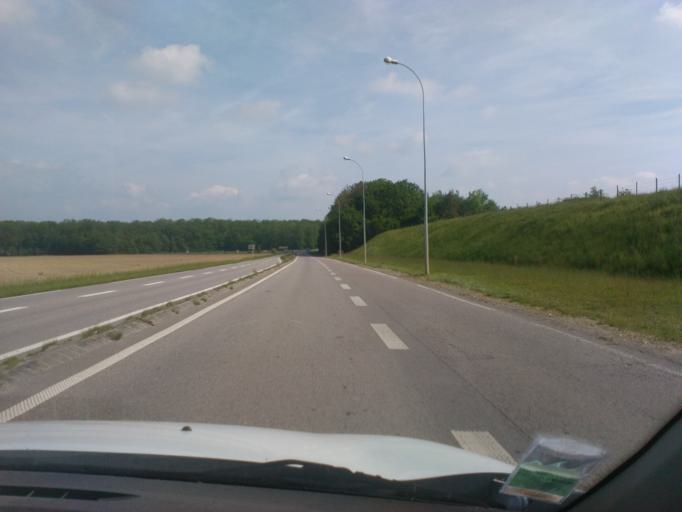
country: FR
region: Lorraine
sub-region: Departement des Vosges
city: Golbey
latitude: 48.2080
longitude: 6.4191
